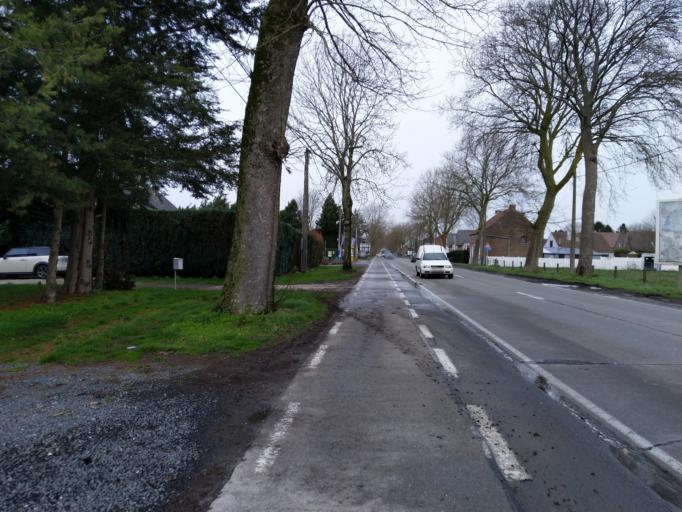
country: BE
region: Wallonia
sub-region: Province du Hainaut
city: Jurbise
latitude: 50.5184
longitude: 3.9197
